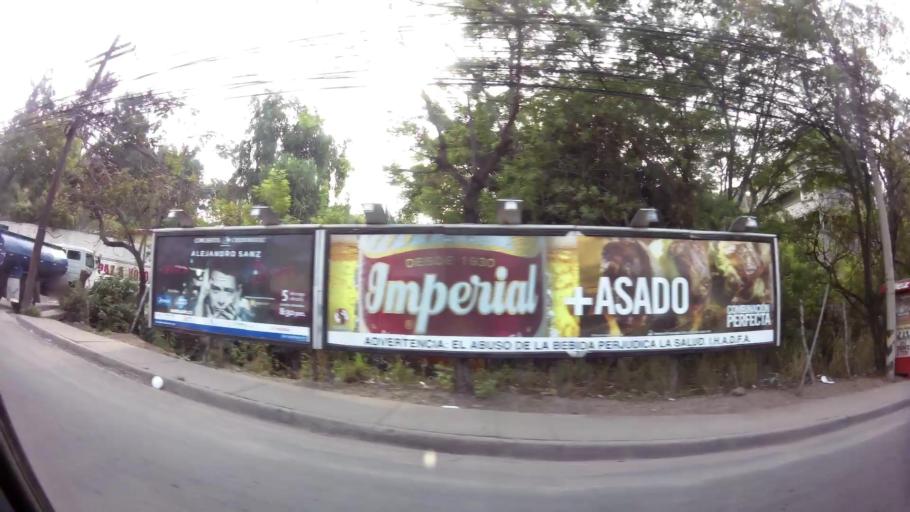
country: HN
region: Francisco Morazan
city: El Tablon
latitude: 14.0572
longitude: -87.1817
